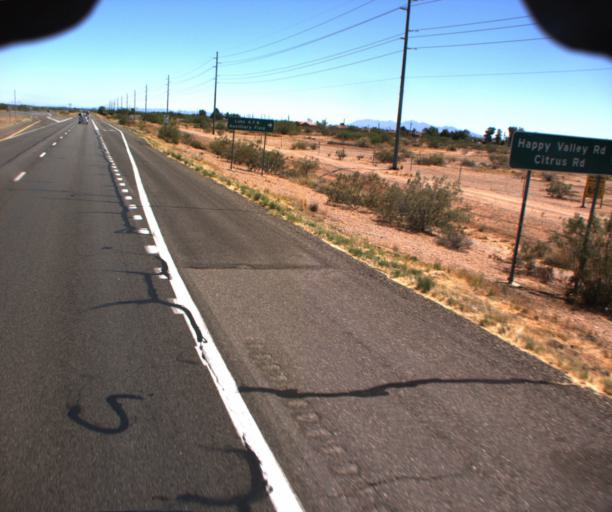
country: US
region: Arizona
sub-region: Maricopa County
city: Sun City West
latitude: 33.7153
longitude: -112.4487
